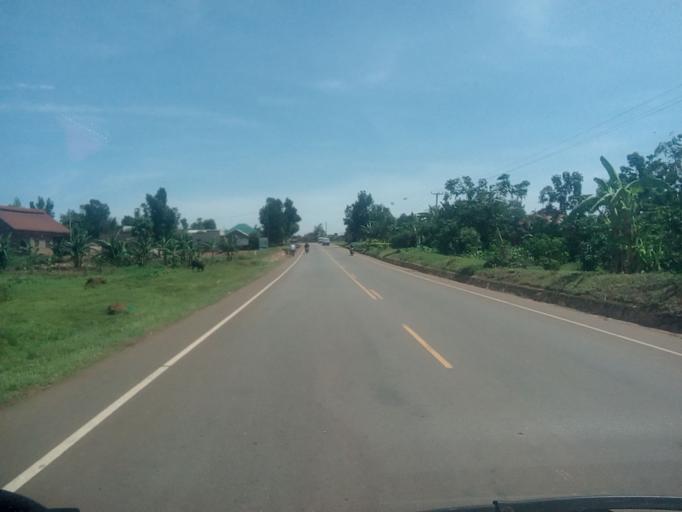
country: UG
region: Eastern Region
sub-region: Jinja District
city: Buwenge
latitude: 0.7778
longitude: 33.1456
